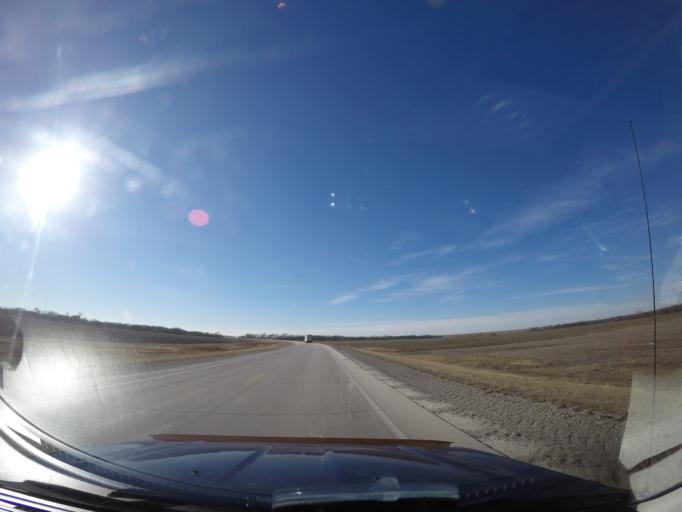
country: US
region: Kansas
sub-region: Marion County
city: Marion
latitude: 38.3630
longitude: -97.0616
